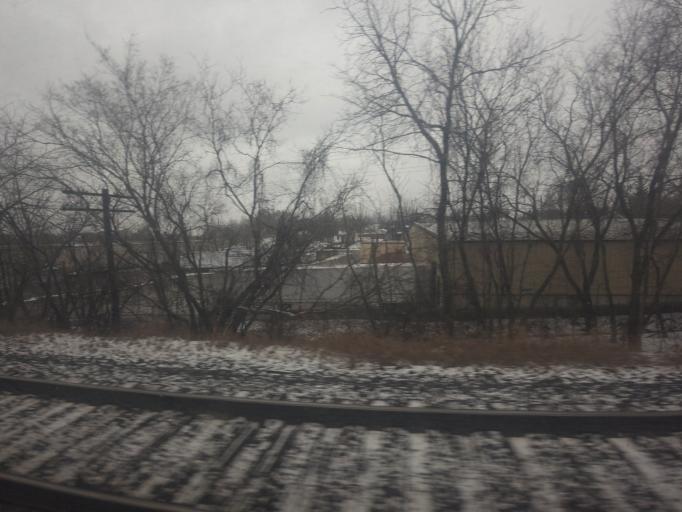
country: CA
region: Ontario
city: Belleville
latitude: 44.1716
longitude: -77.3979
